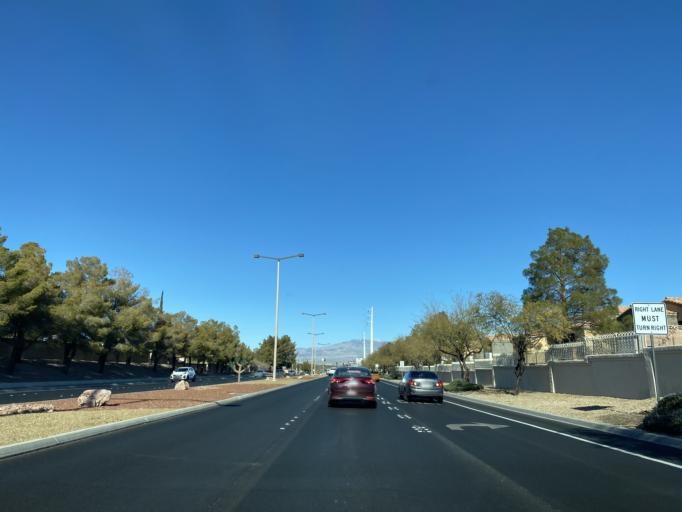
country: US
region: Nevada
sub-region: Clark County
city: Summerlin South
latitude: 36.2159
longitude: -115.2787
